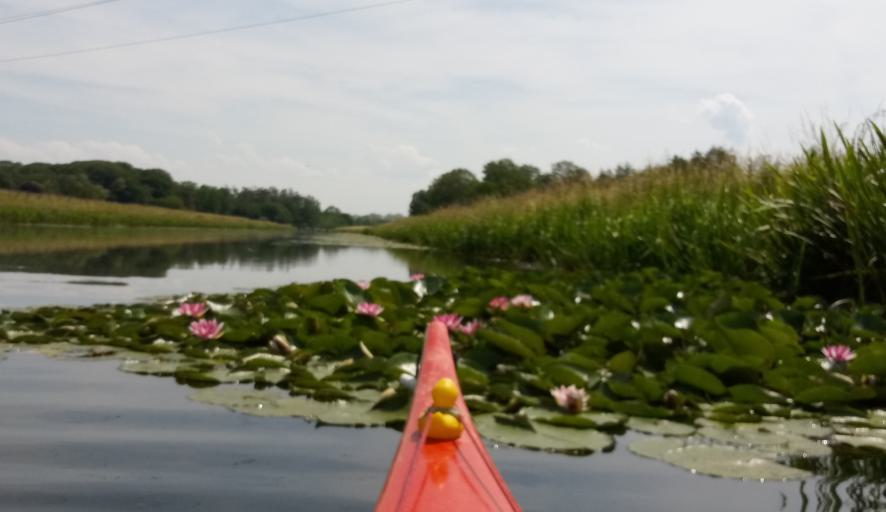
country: NL
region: Gelderland
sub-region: Gemeente Lochem
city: Eefde
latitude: 52.1585
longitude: 6.2350
